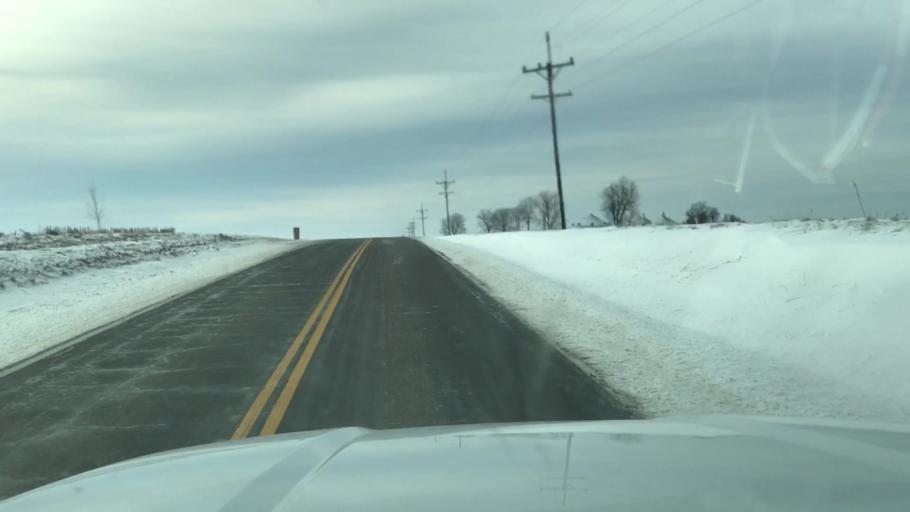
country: US
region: Missouri
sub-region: Holt County
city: Mound City
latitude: 40.1041
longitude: -95.1449
